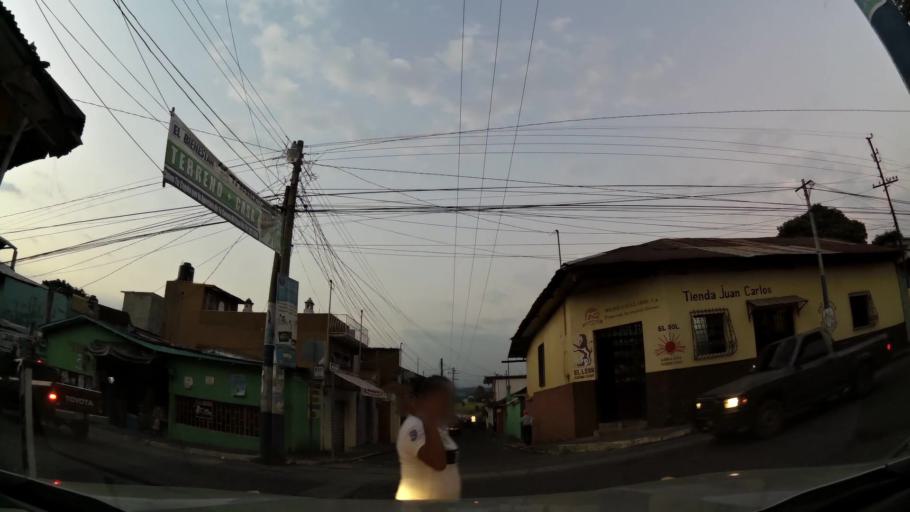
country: GT
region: Retalhuleu
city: San Felipe
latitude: 14.6251
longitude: -91.5950
